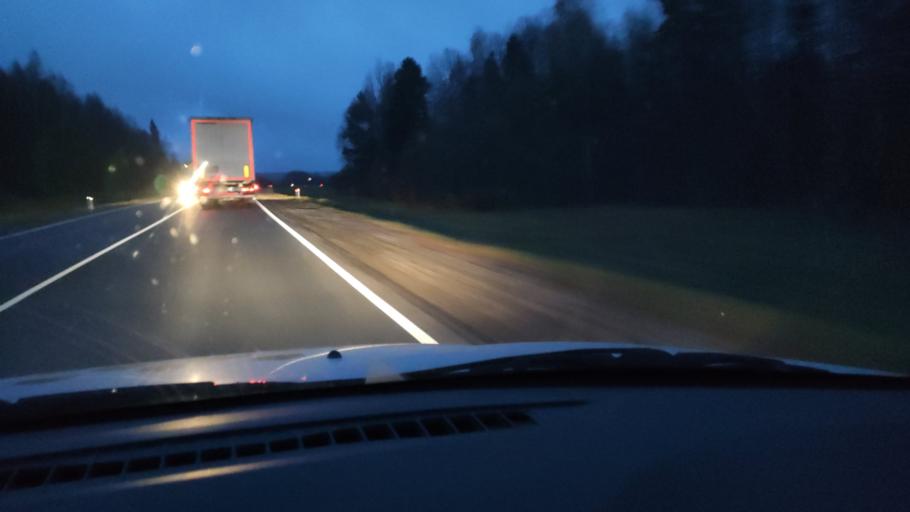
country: RU
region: Kirov
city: Kostino
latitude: 58.8136
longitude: 53.5901
